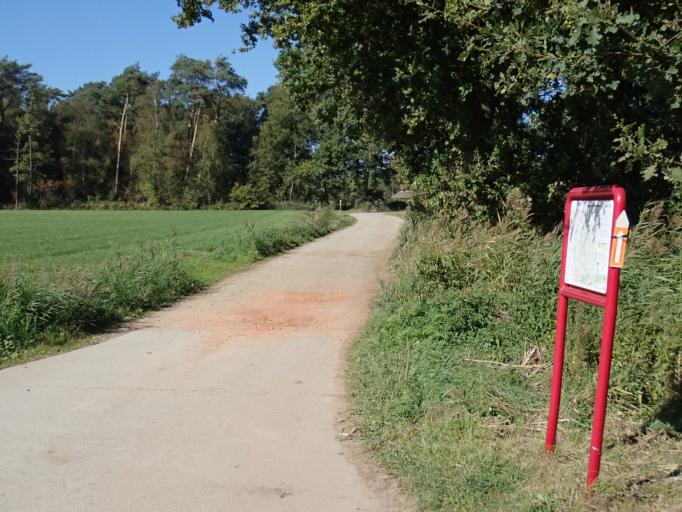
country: BE
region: Flanders
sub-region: Provincie Antwerpen
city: Baarle-Hertog
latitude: 51.4119
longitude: 4.8474
